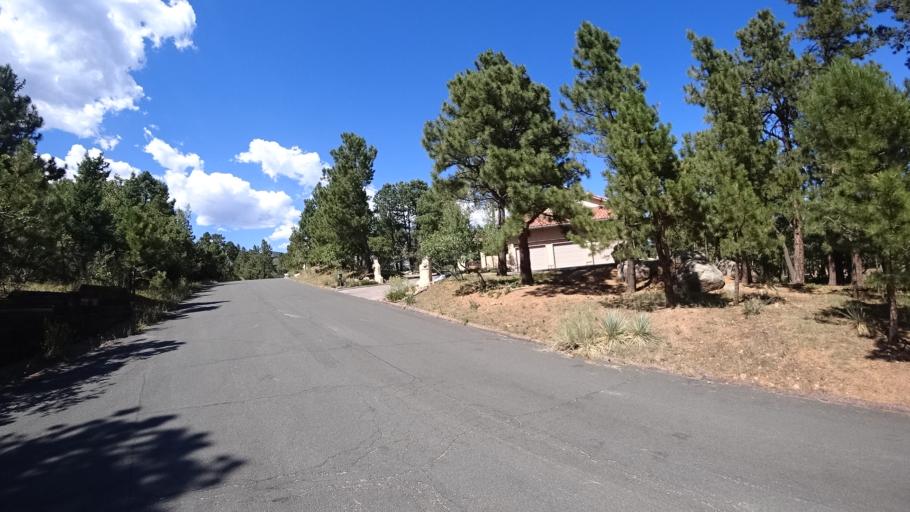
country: US
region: Colorado
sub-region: El Paso County
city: Colorado Springs
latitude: 38.7802
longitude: -104.8588
